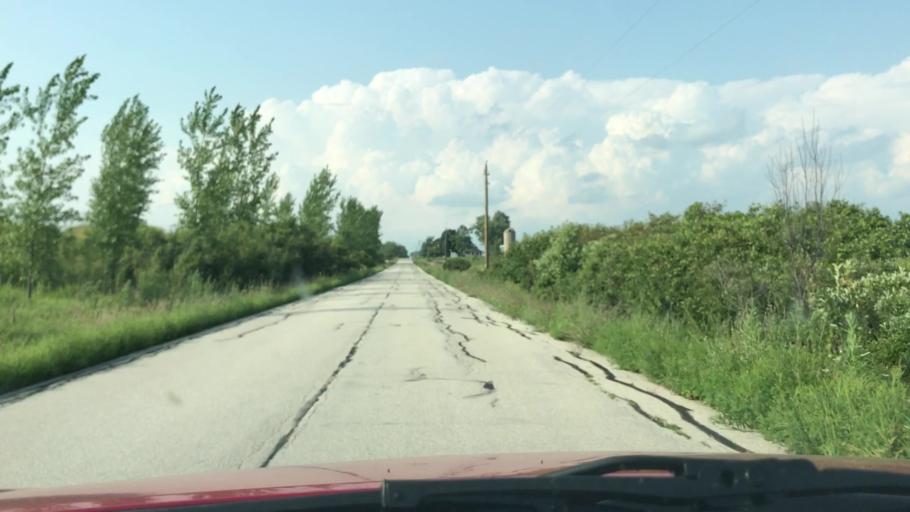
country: US
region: Wisconsin
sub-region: Brown County
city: Oneida
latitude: 44.4400
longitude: -88.1704
